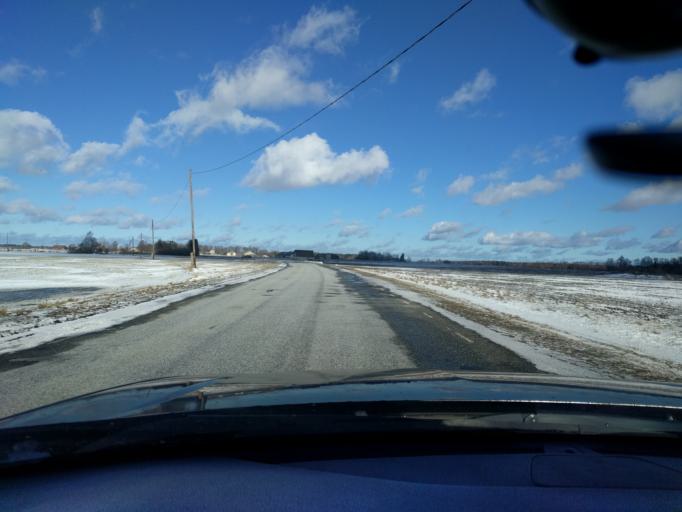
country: EE
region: Harju
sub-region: Raasiku vald
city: Raasiku
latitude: 59.3253
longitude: 25.1602
